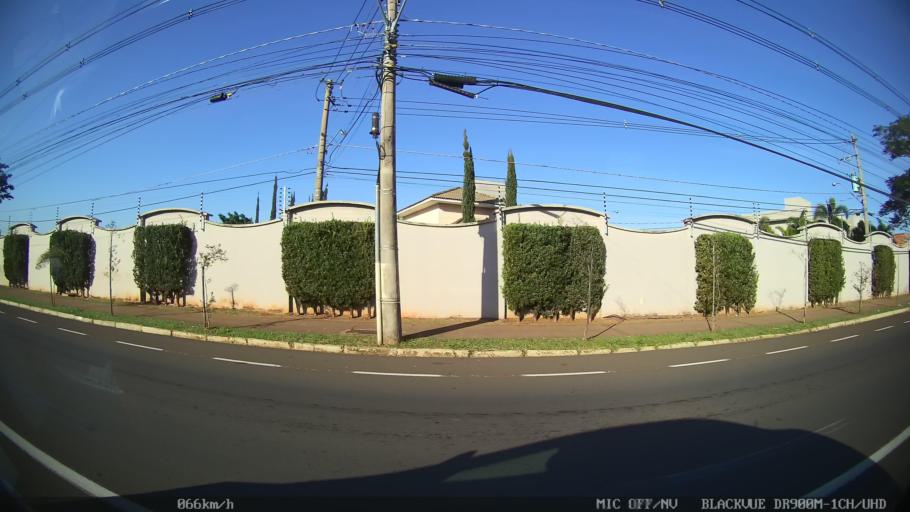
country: BR
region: Sao Paulo
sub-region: Sao Jose Do Rio Preto
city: Sao Jose do Rio Preto
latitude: -20.8620
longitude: -49.4119
